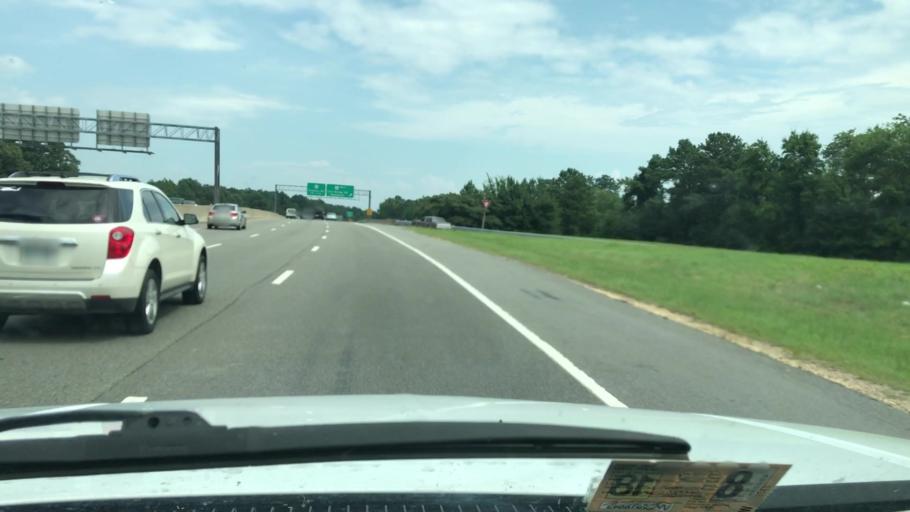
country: US
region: Virginia
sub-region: Chesterfield County
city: Bensley
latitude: 37.4511
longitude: -77.4882
